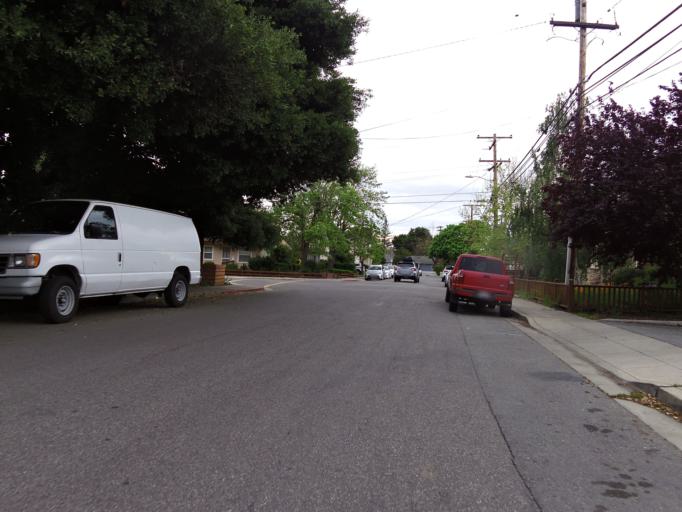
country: US
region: California
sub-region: Santa Clara County
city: Mountain View
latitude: 37.3935
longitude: -122.0936
